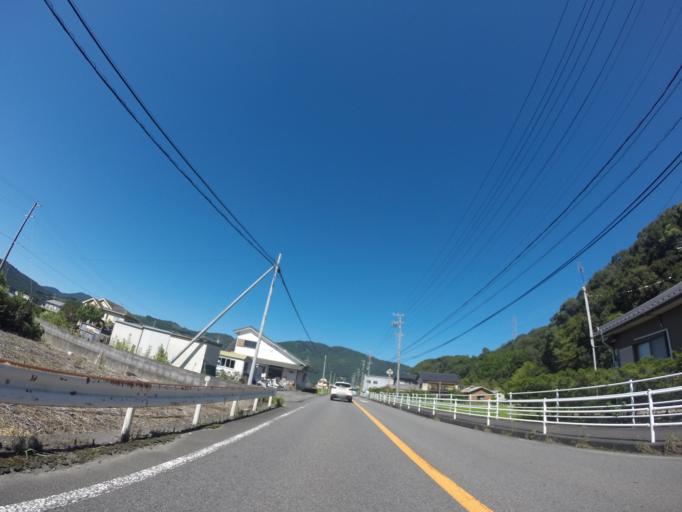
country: JP
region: Shizuoka
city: Kanaya
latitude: 34.8684
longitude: 138.1216
